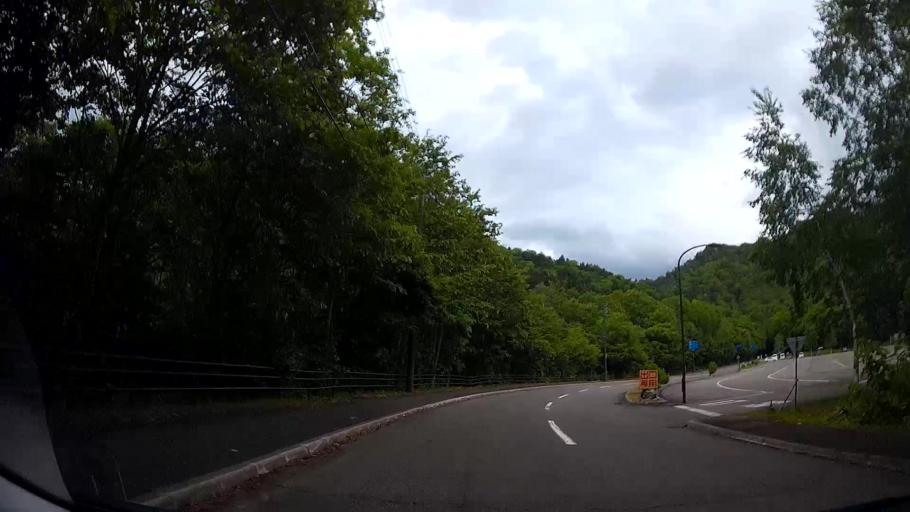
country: JP
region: Hokkaido
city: Sapporo
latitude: 42.9307
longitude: 141.1596
